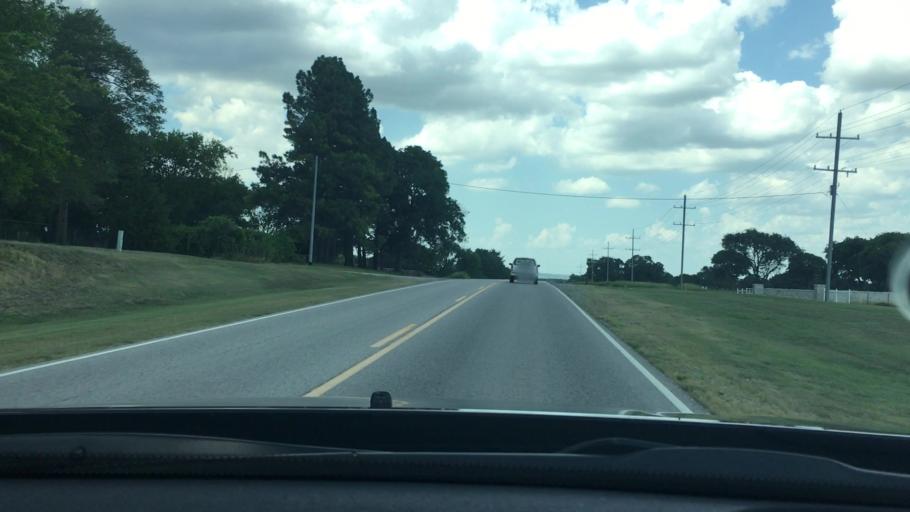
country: US
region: Oklahoma
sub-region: Pontotoc County
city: Ada
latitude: 34.6715
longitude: -96.6349
